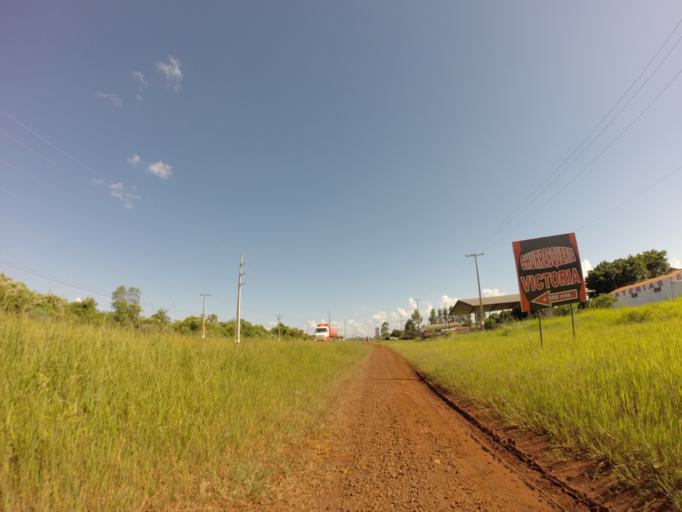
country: PY
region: Alto Parana
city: Ciudad del Este
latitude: -25.3705
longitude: -54.6450
